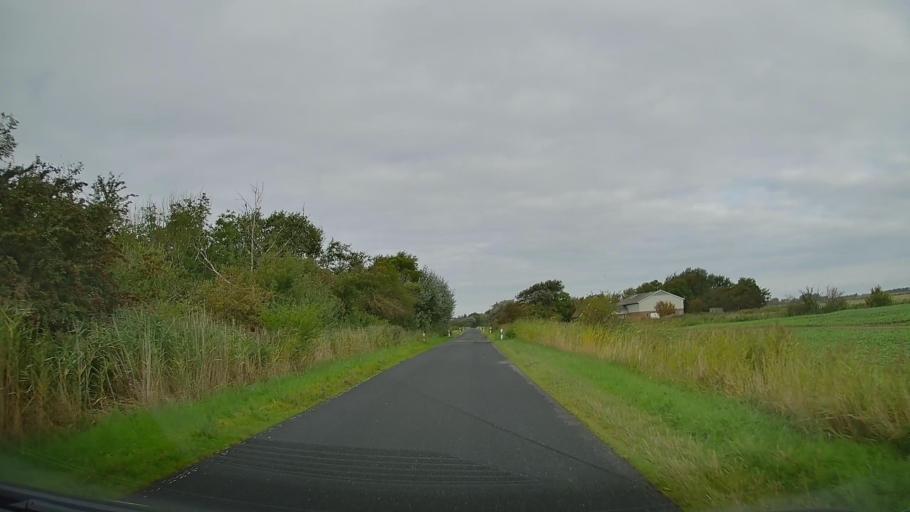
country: DE
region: Schleswig-Holstein
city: Emmelsbull-Horsbull
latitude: 54.8118
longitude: 8.6526
